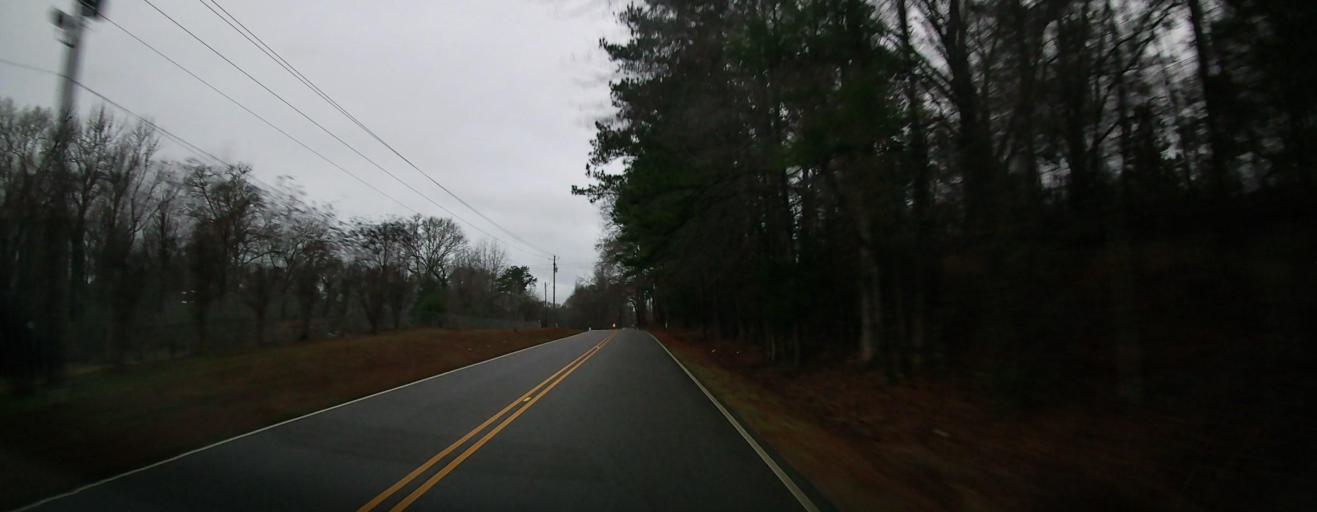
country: US
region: Alabama
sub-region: Tuscaloosa County
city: Vance
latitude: 33.1178
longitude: -87.2222
